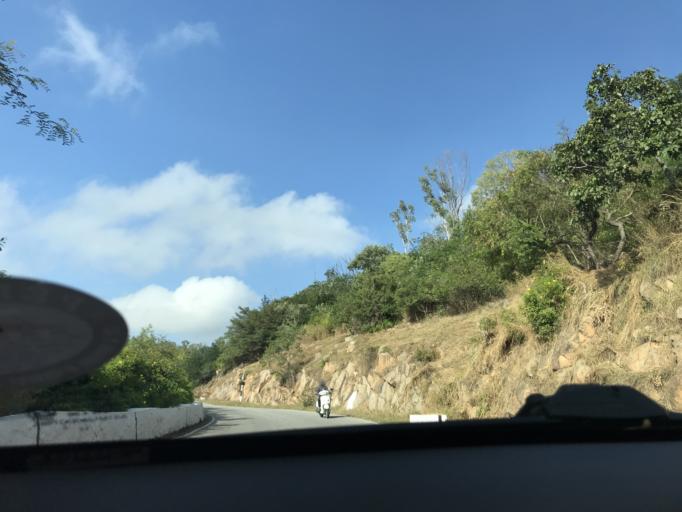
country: IN
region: Karnataka
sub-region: Mysore
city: Mysore
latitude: 12.2823
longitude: 76.6923
